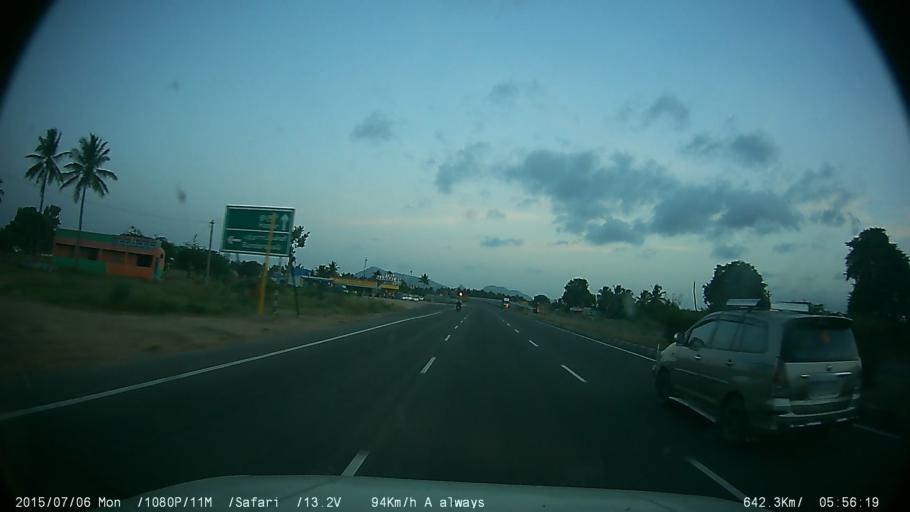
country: IN
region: Tamil Nadu
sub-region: Krishnagiri
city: Krishnagiri
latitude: 12.5727
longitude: 78.1705
